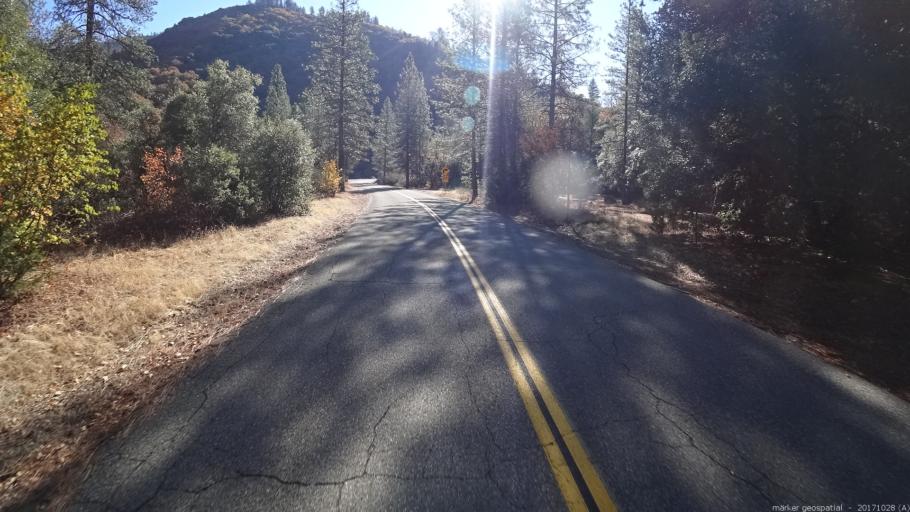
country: US
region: California
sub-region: Trinity County
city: Lewiston
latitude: 40.7777
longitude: -122.6116
